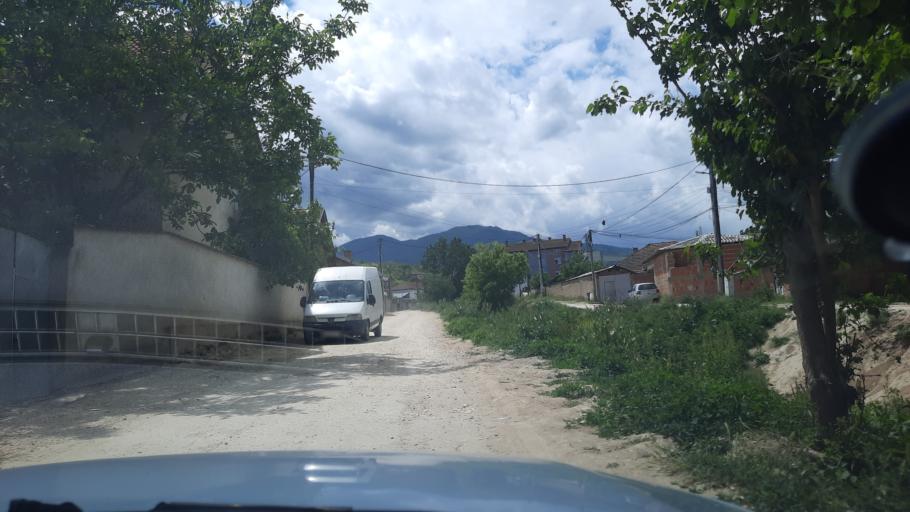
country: MK
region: Studenicani
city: Studenichani
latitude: 41.9222
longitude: 21.5359
